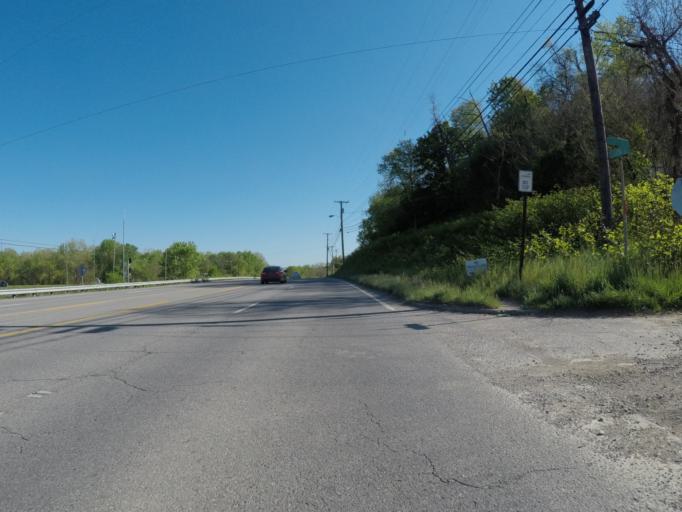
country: US
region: Kentucky
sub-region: Boyd County
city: Catlettsburg
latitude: 38.3997
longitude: -82.6011
